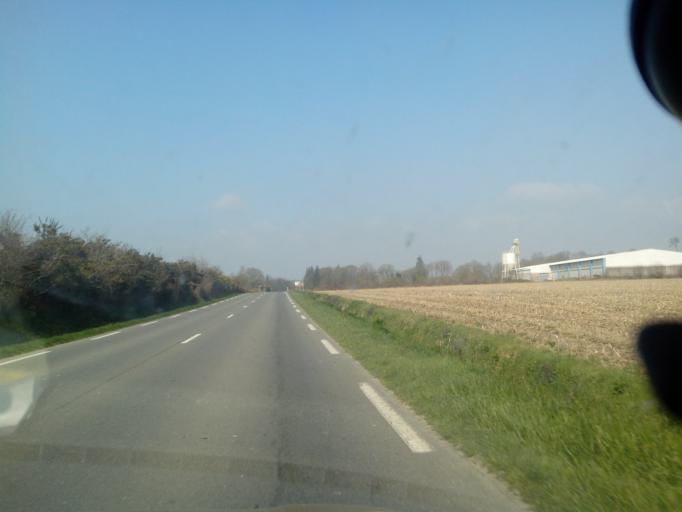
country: FR
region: Brittany
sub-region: Departement d'Ille-et-Vilaine
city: Saint-Meen-le-Grand
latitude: 48.2194
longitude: -2.1774
